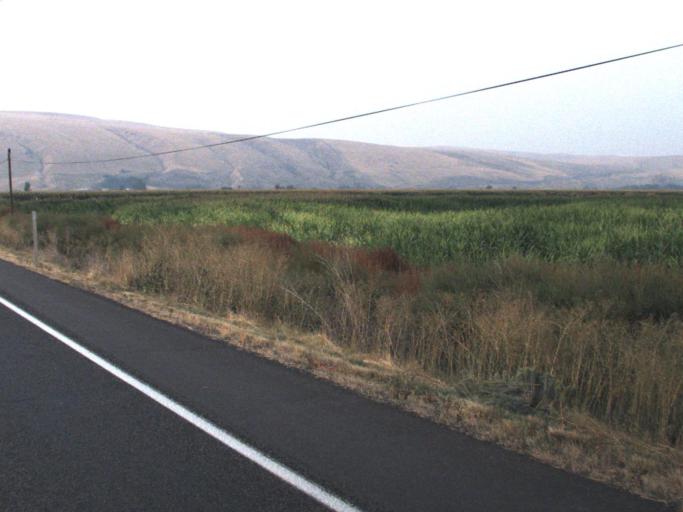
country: US
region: Washington
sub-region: Yakima County
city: Toppenish
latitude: 46.3257
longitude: -120.3204
